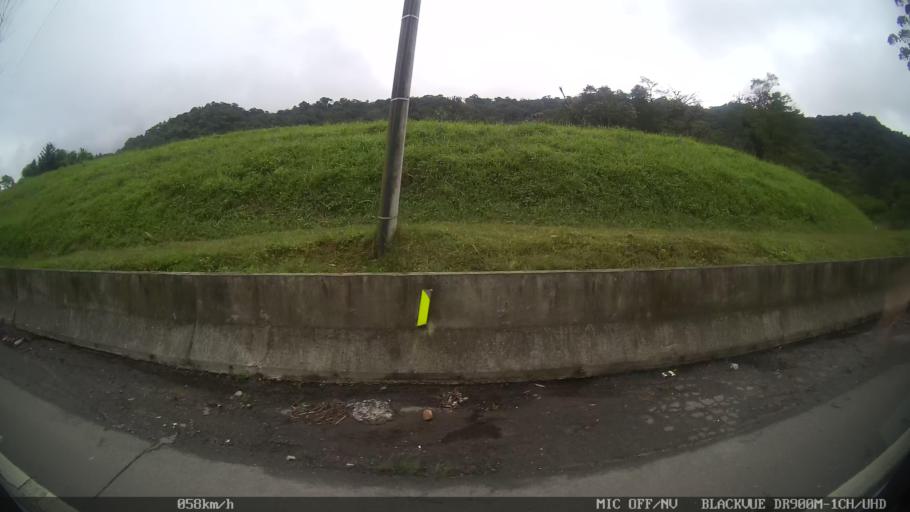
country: BR
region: Parana
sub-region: Guaratuba
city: Guaratuba
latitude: -25.8606
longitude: -48.9374
